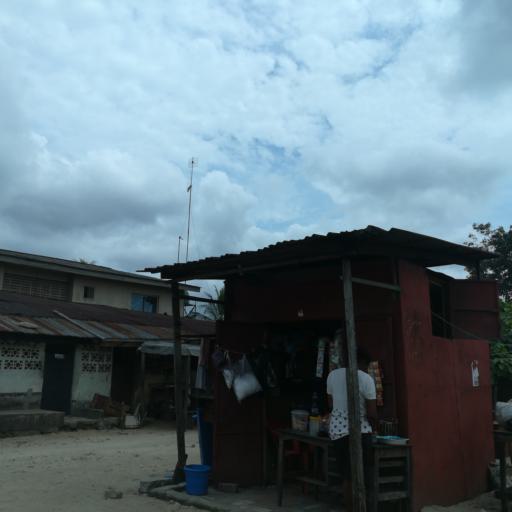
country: NG
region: Rivers
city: Port Harcourt
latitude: 4.7936
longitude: 7.0253
